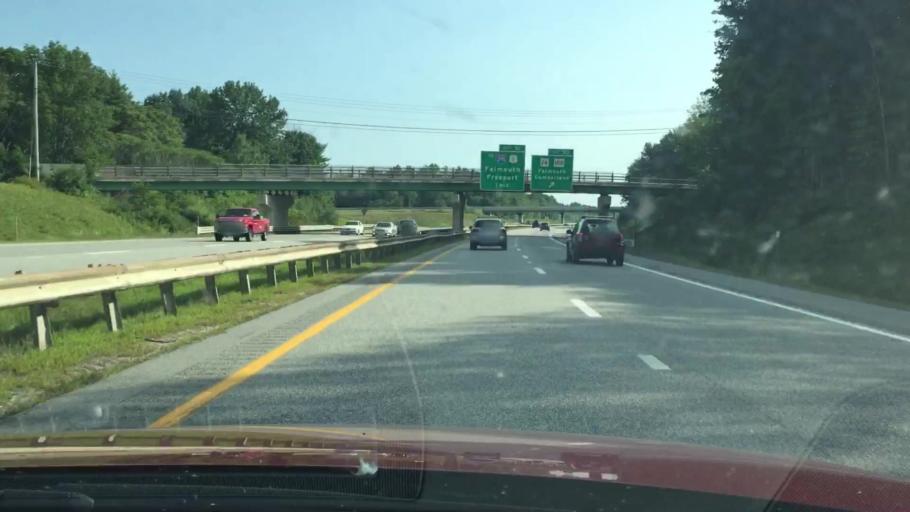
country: US
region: Maine
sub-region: Cumberland County
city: Falmouth
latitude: 43.7354
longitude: -70.3020
